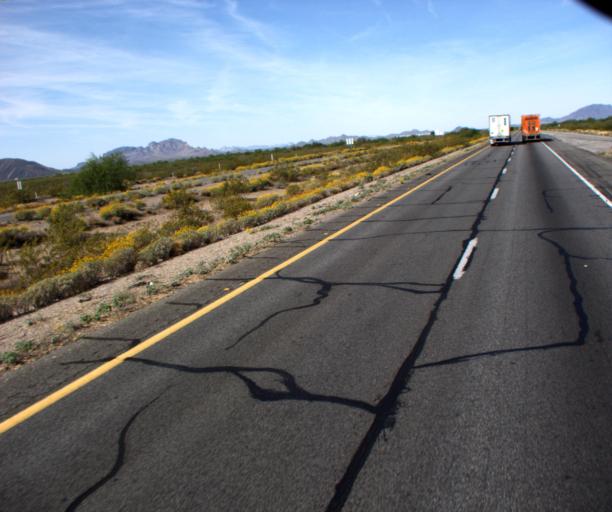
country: US
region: Arizona
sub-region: Maricopa County
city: Buckeye
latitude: 33.4829
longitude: -112.8715
